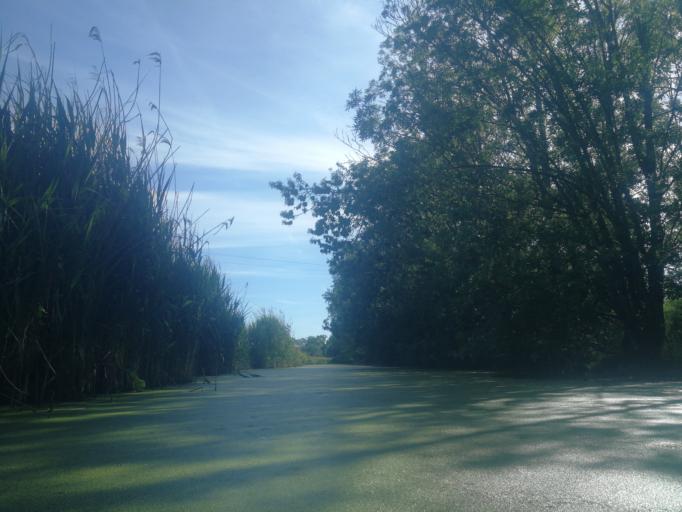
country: FR
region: Poitou-Charentes
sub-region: Departement de la Charente-Maritime
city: Marans
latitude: 46.3673
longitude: -0.9619
